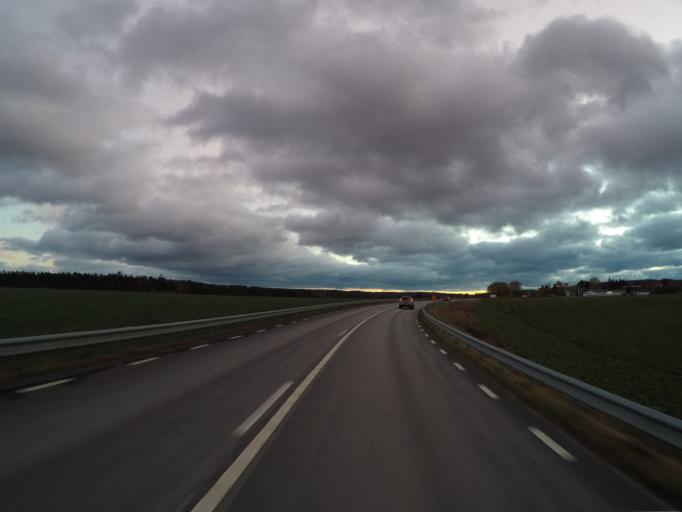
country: SE
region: Skane
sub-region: Kristianstads Kommun
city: Degeberga
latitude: 55.8448
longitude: 14.0964
